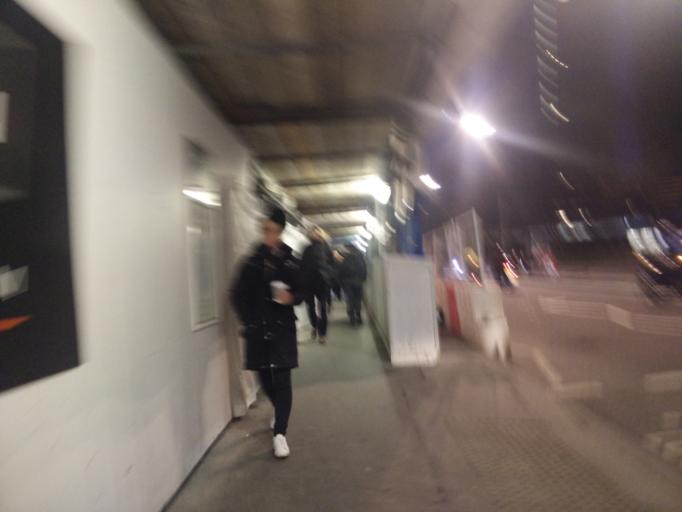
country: GB
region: England
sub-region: Greater London
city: Barbican
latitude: 51.5187
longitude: -0.0972
